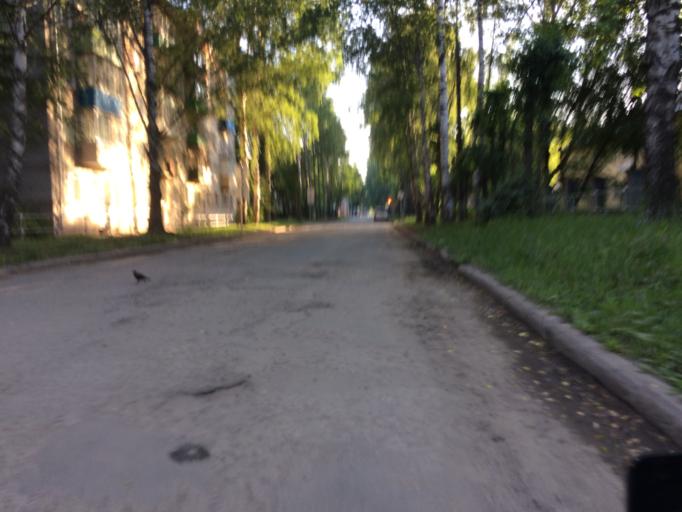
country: RU
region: Mariy-El
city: Yoshkar-Ola
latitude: 56.6463
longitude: 47.8814
